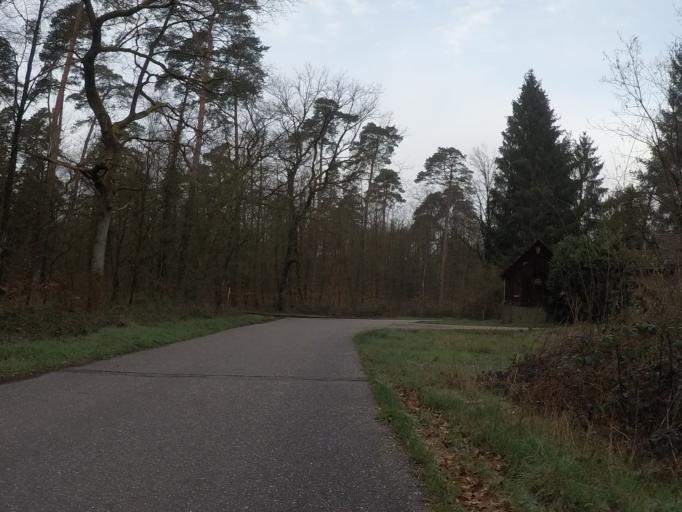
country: DE
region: Rheinland-Pfalz
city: Kandel
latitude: 49.0688
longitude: 8.2238
